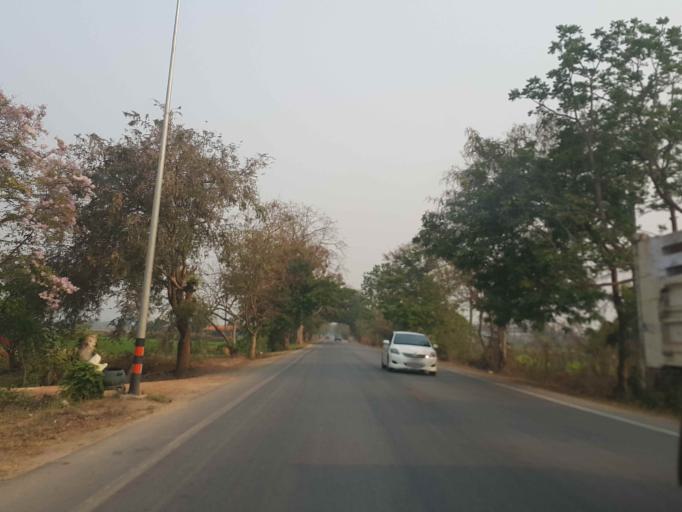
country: TH
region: Chiang Mai
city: Mae Taeng
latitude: 19.0496
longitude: 98.9627
